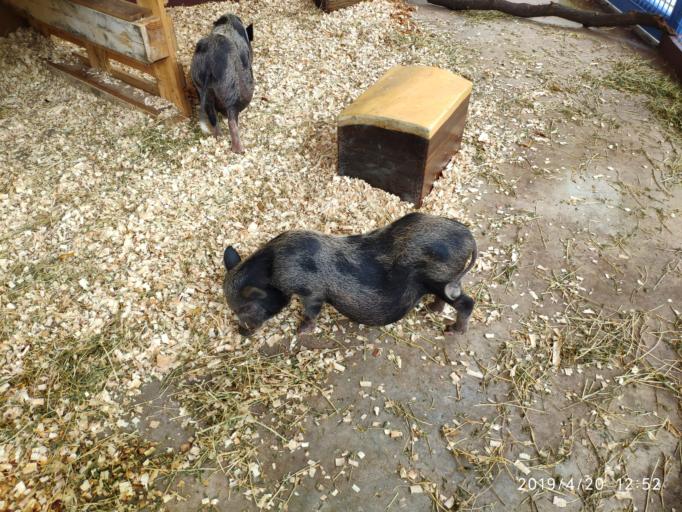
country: MY
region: Johor
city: Johor Bahru
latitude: 1.4033
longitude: 103.7967
